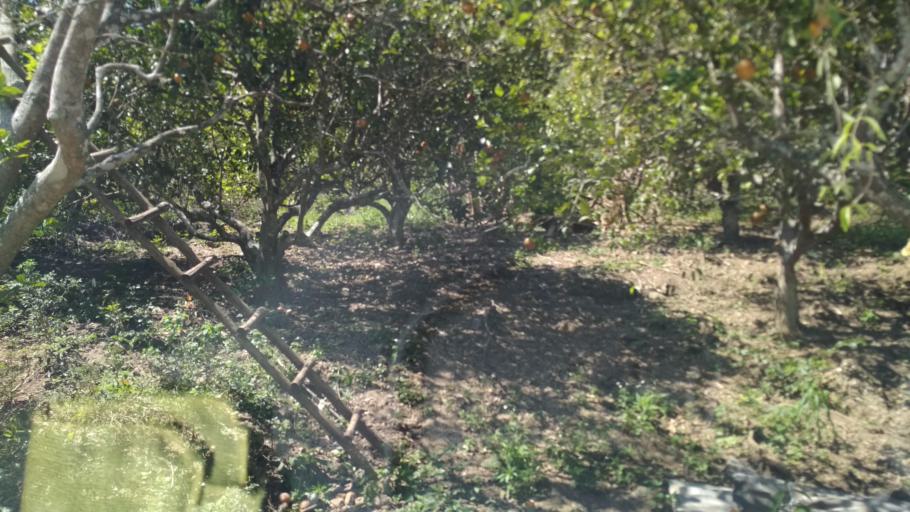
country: MX
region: Veracruz
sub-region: Papantla
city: Polutla
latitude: 20.4871
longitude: -97.2260
